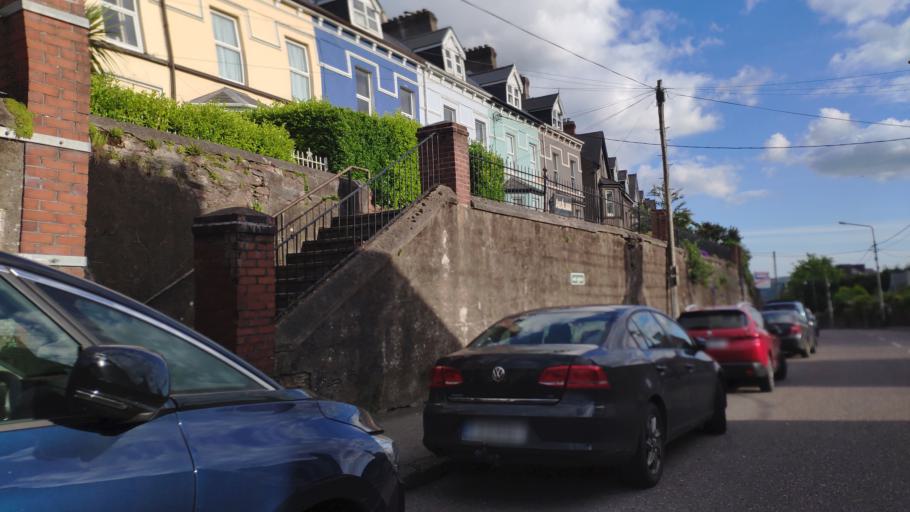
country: IE
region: Munster
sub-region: County Cork
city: Cork
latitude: 51.9065
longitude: -8.4578
